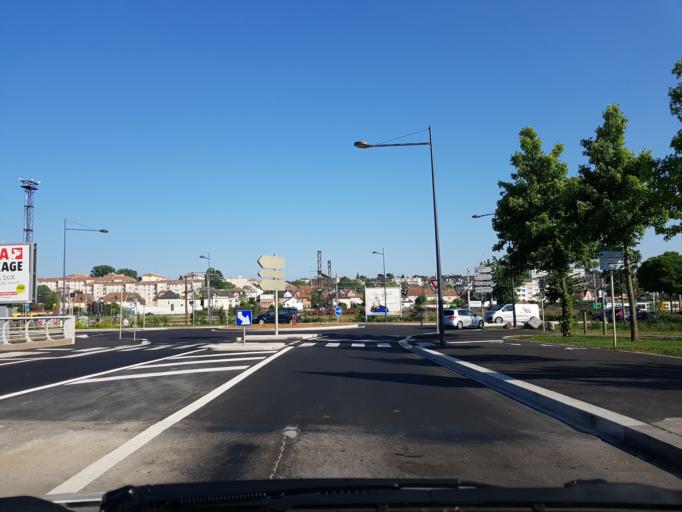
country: FR
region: Alsace
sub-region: Departement du Haut-Rhin
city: Riedisheim
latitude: 47.7513
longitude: 7.3580
